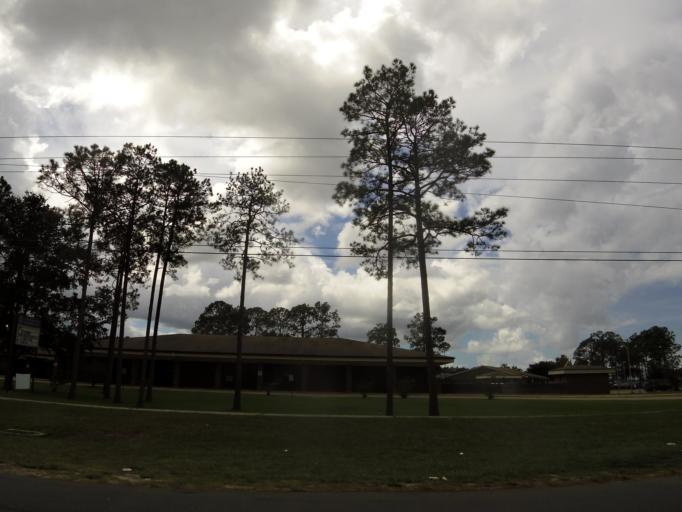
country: US
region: Florida
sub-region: Clay County
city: Middleburg
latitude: 30.0823
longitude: -81.9401
